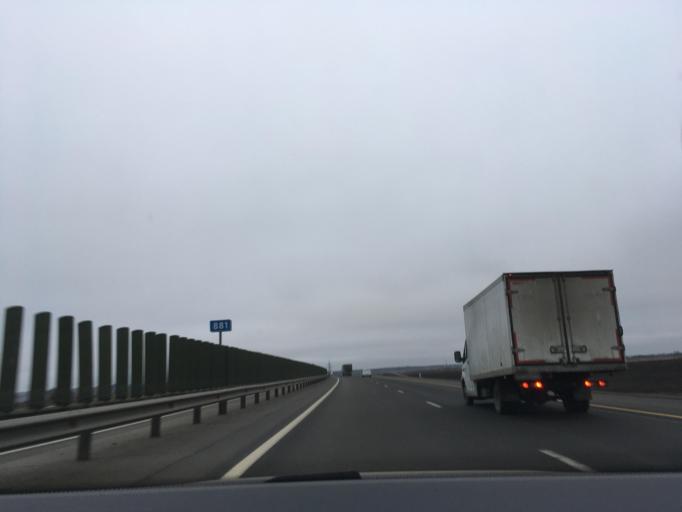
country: RU
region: Rostov
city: Tarasovskiy
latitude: 48.7429
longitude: 40.3937
